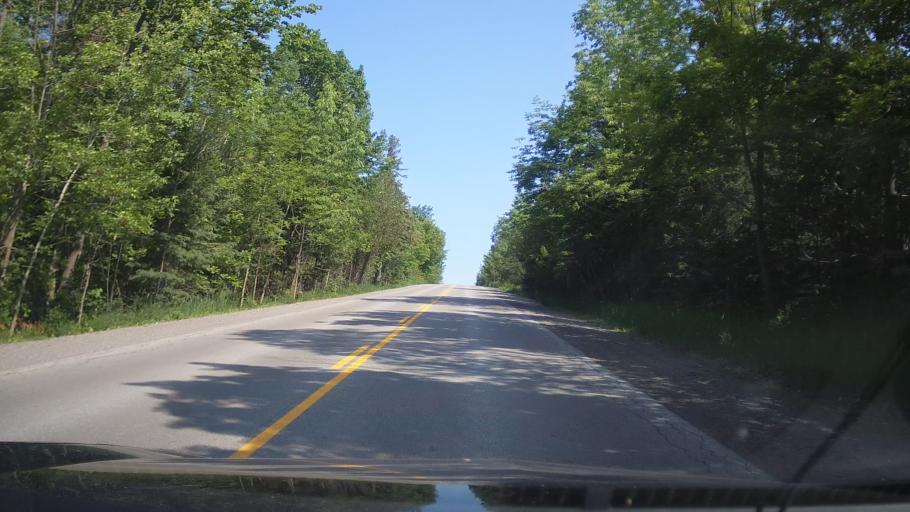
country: CA
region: Ontario
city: Uxbridge
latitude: 44.5051
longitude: -78.9531
